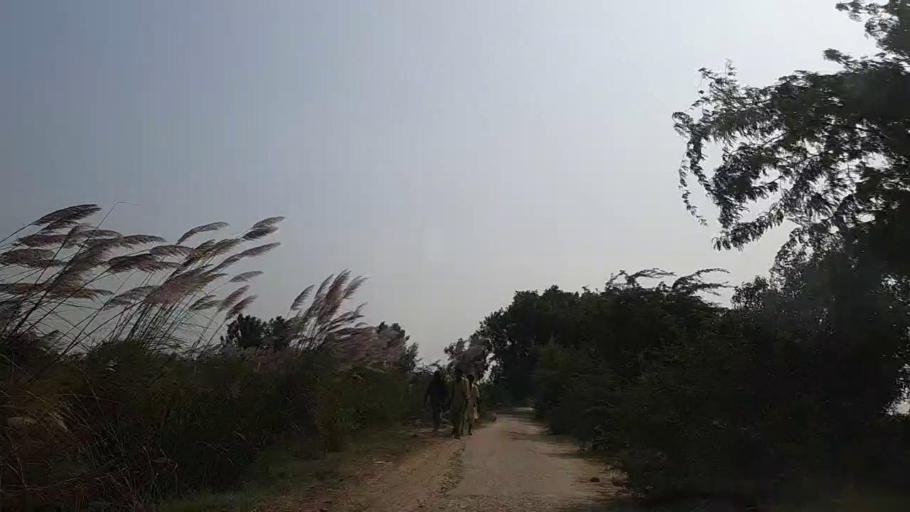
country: PK
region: Sindh
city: Mirpur Sakro
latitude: 24.5926
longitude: 67.7182
